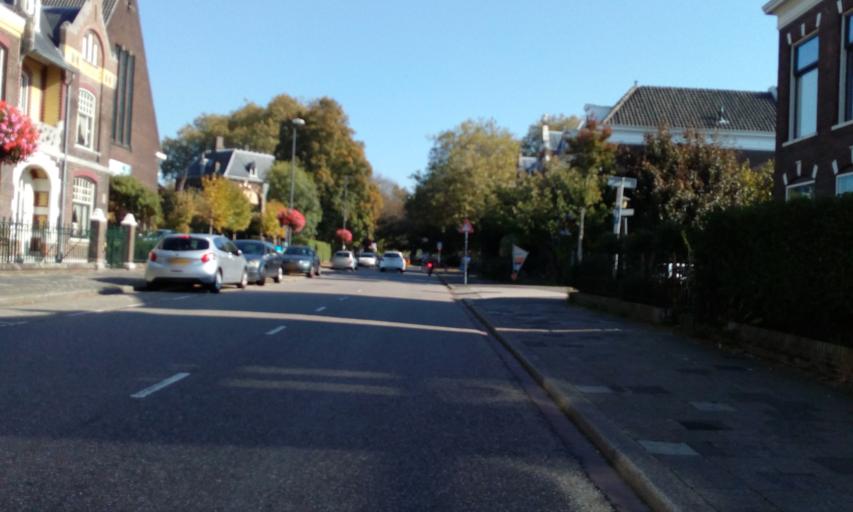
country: NL
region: South Holland
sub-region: Gemeente Vlaardingen
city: Vlaardingen
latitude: 51.9094
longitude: 4.3500
